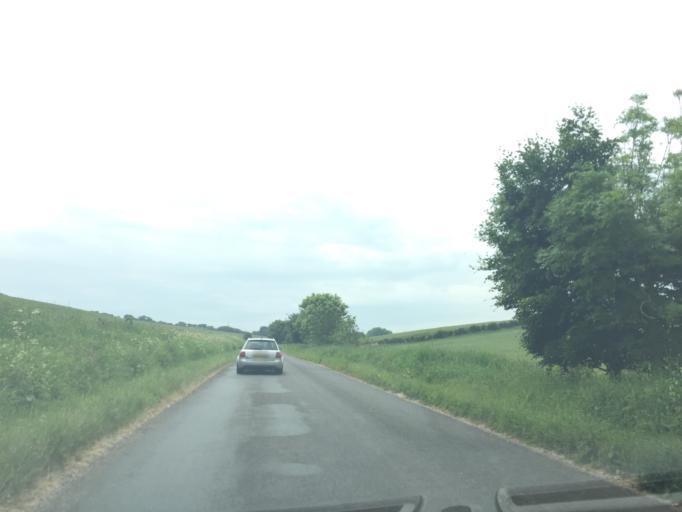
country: GB
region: England
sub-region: Dorset
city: Wool
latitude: 50.6360
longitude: -2.2671
